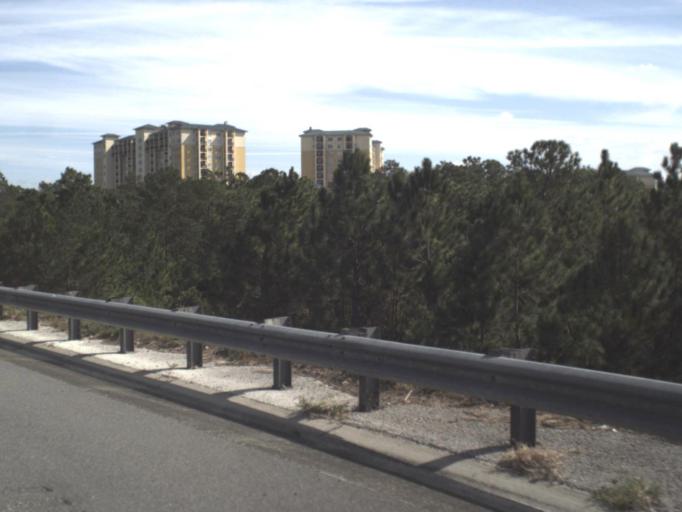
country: US
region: Florida
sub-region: Osceola County
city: Celebration
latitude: 28.3515
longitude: -81.4911
